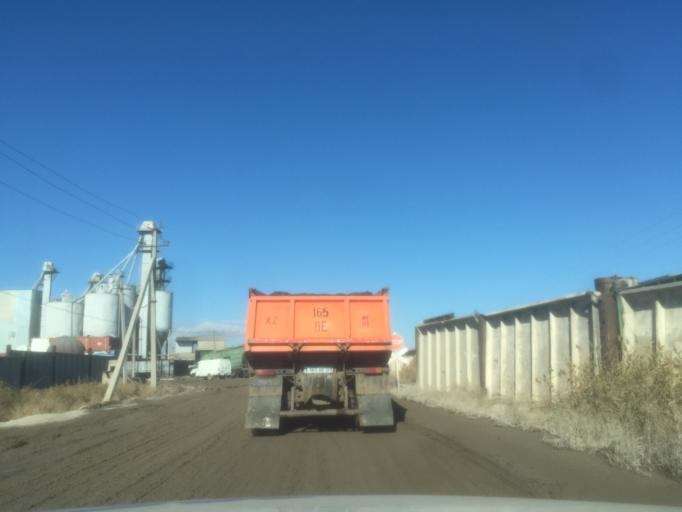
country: KZ
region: Astana Qalasy
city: Astana
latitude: 51.2133
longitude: 71.3509
